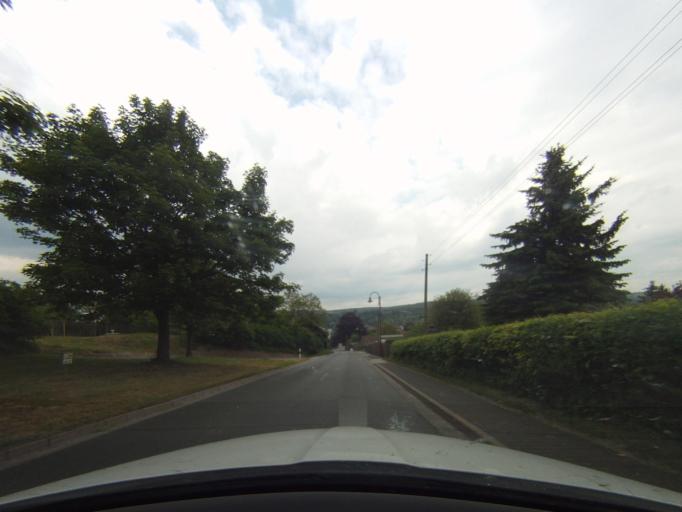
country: DE
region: Thuringia
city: Konigsee
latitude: 50.6572
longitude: 11.0999
